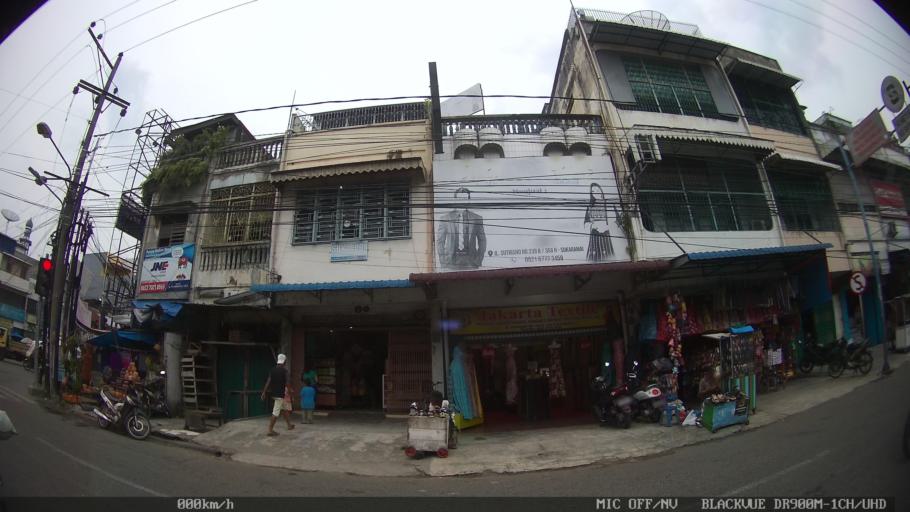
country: ID
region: North Sumatra
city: Medan
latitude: 3.5822
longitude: 98.7036
